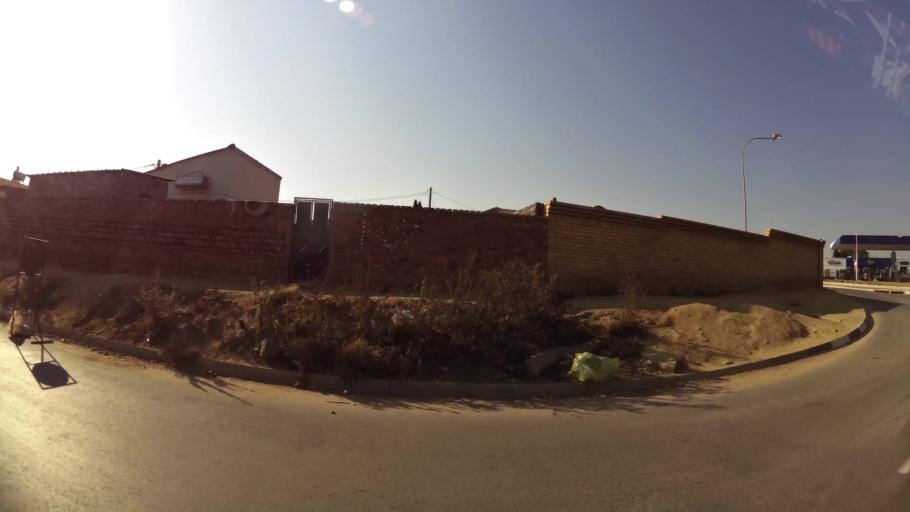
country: ZA
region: Gauteng
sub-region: City of Johannesburg Metropolitan Municipality
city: Modderfontein
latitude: -26.1041
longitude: 28.1171
